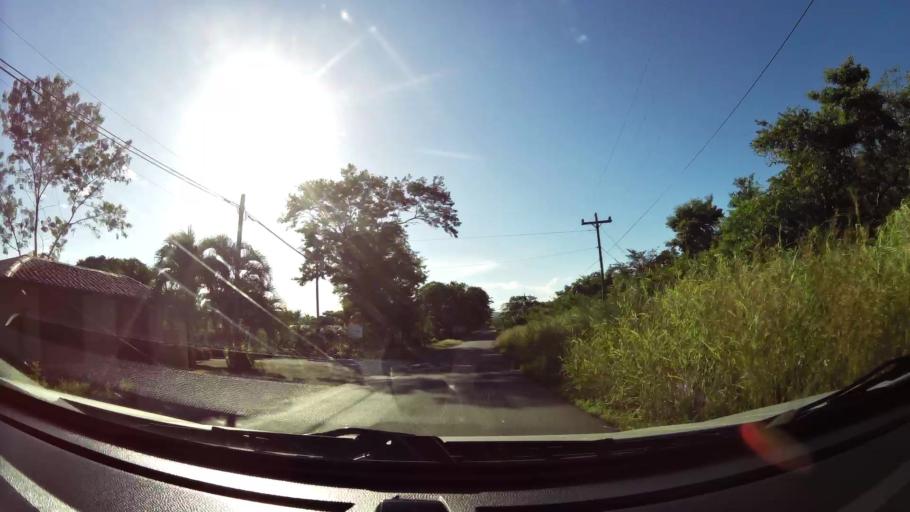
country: CR
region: Guanacaste
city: Sardinal
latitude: 10.4981
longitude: -85.6373
